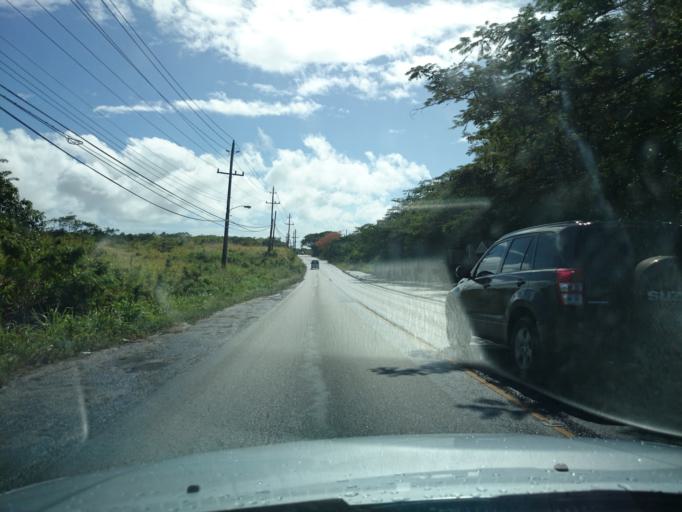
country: BB
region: Saint James
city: Holetown
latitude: 13.1853
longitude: -59.6120
